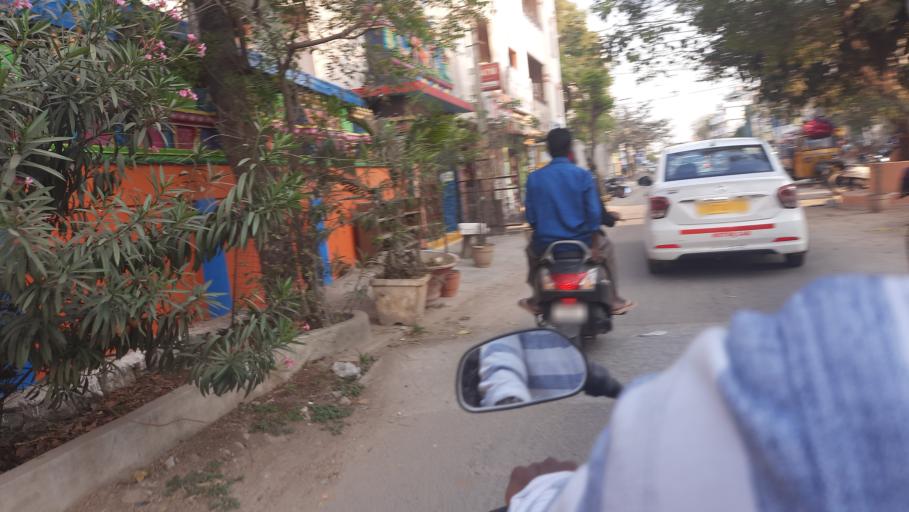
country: IN
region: Telangana
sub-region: Rangareddi
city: Secunderabad
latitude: 17.4933
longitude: 78.5465
